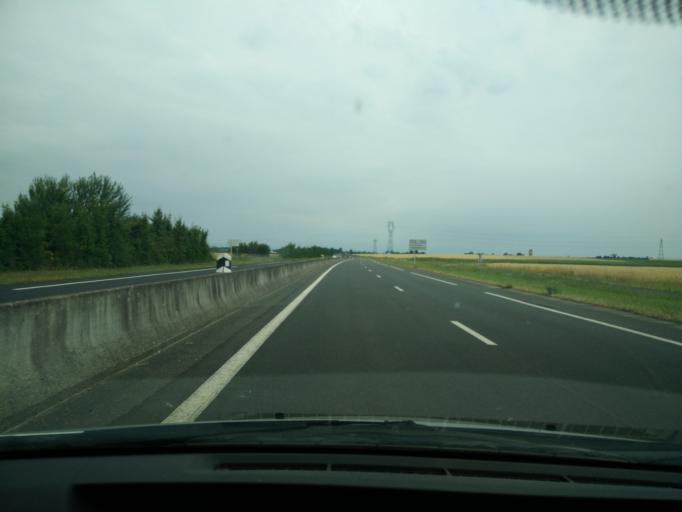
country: FR
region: Pays de la Loire
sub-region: Departement de Maine-et-Loire
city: Doue-la-Fontaine
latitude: 47.2223
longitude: -0.3070
